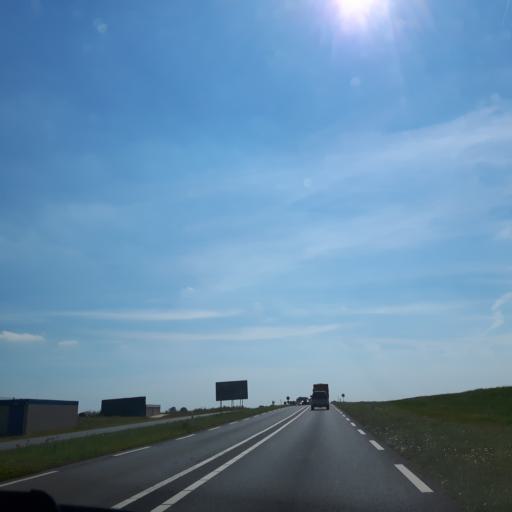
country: NL
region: North Brabant
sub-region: Gemeente Steenbergen
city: Nieuw-Vossemeer
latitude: 51.6152
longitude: 4.1777
